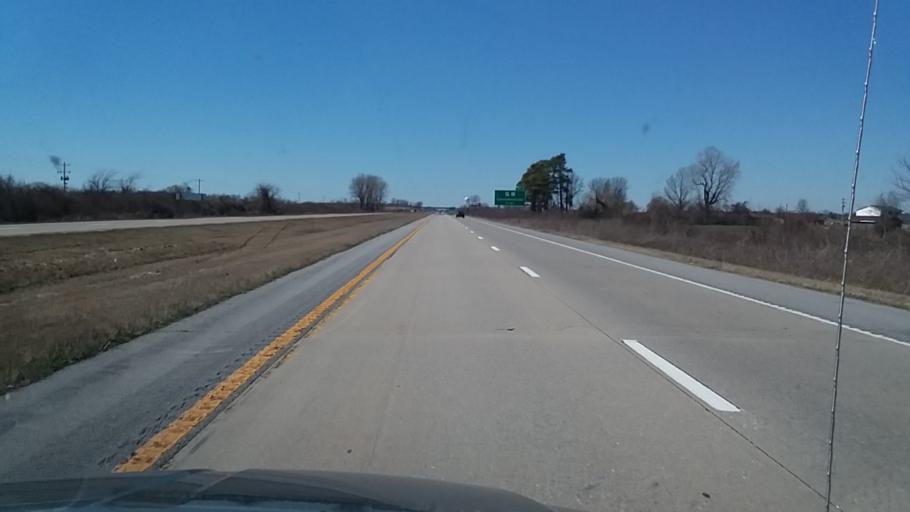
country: US
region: Missouri
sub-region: Pemiscot County
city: Caruthersville
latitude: 36.1450
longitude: -89.6483
